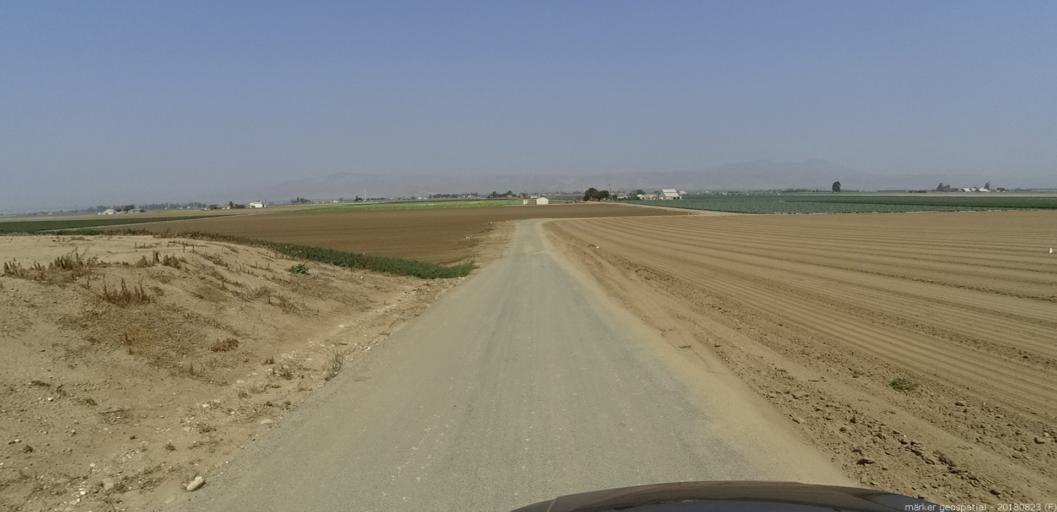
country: US
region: California
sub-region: Monterey County
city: Soledad
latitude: 36.3851
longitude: -121.3578
